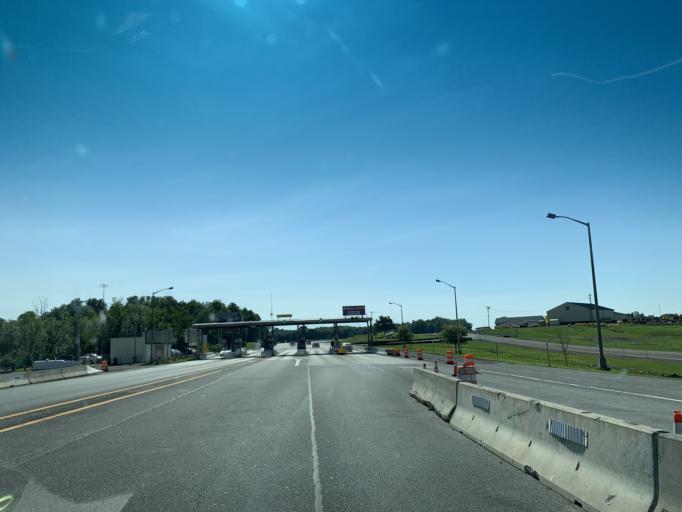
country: US
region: New York
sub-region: Oneida County
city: Sherrill
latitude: 43.1207
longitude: -75.5853
